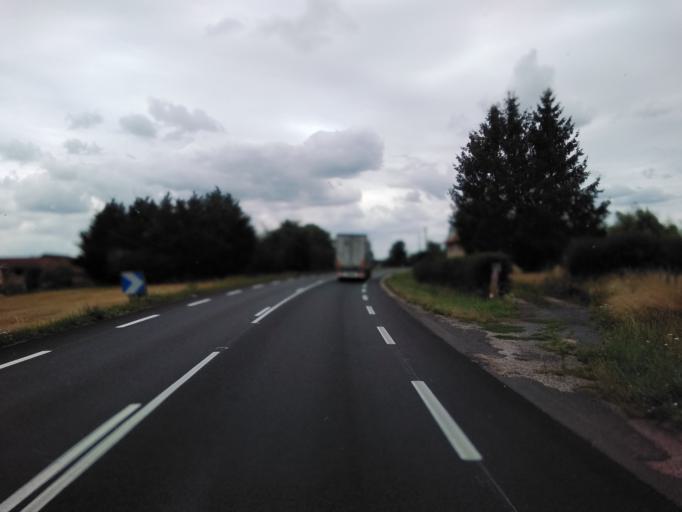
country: FR
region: Rhone-Alpes
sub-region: Departement de l'Ain
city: Coligny
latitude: 46.3563
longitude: 5.3289
